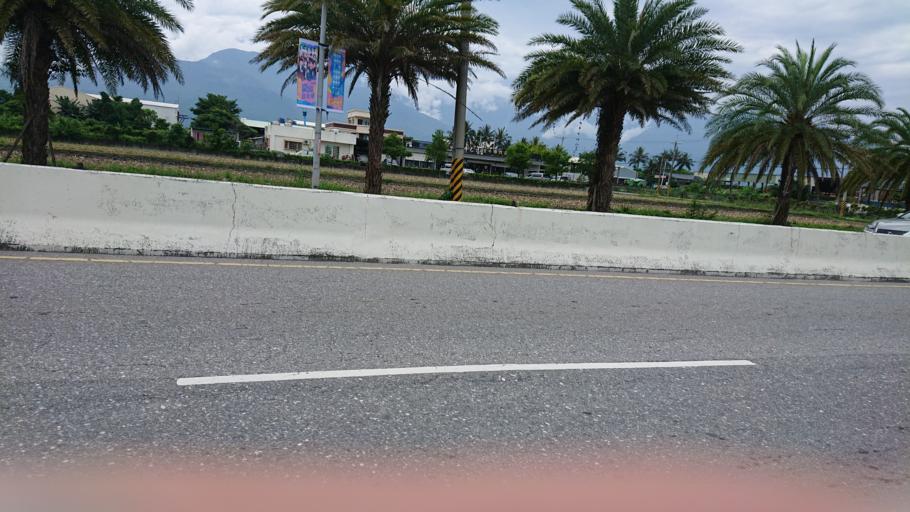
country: TW
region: Taiwan
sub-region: Hualien
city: Hualian
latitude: 23.9456
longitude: 121.5970
